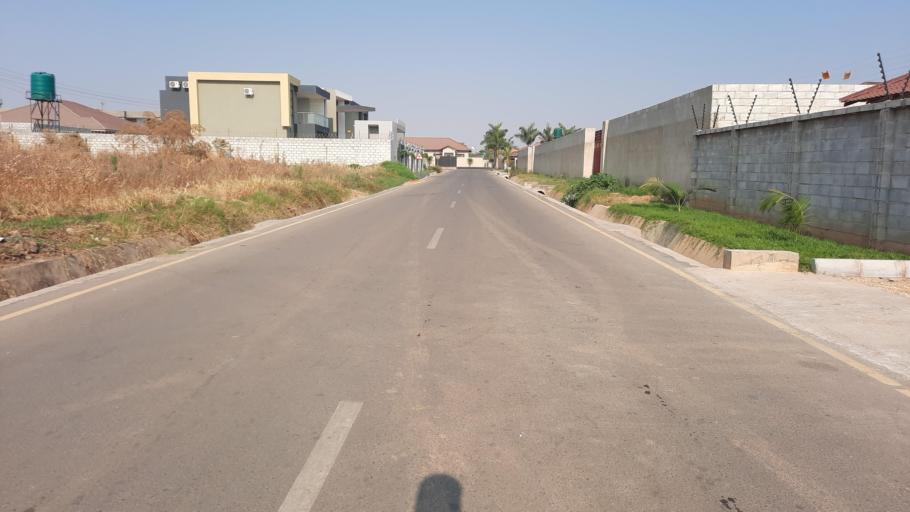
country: ZM
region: Lusaka
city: Lusaka
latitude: -15.3908
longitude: 28.3883
